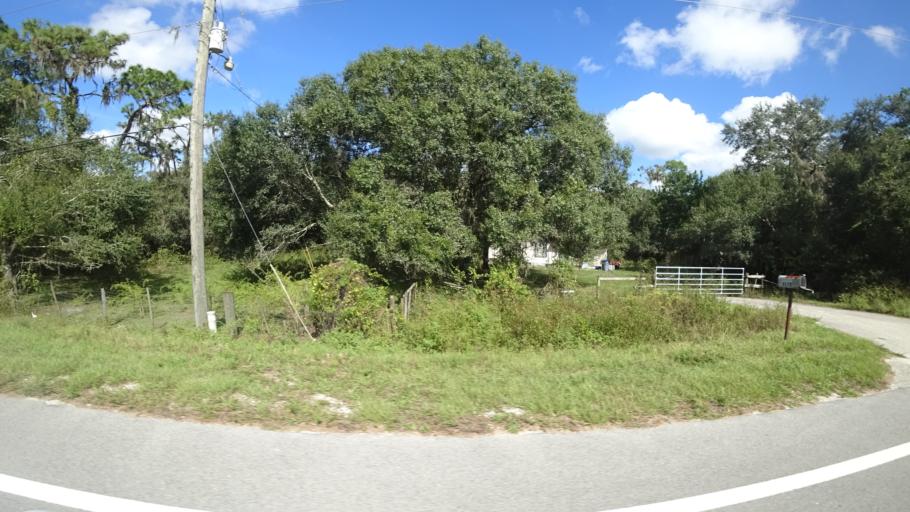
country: US
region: Florida
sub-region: Sarasota County
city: Lake Sarasota
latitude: 27.3681
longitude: -82.1451
